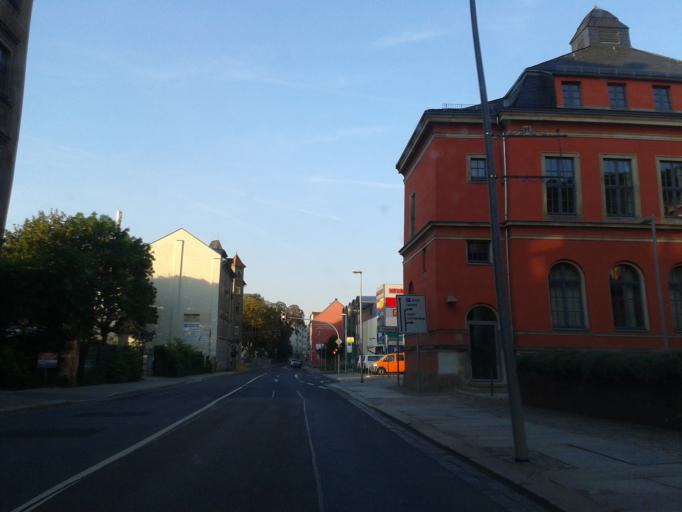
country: DE
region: Saxony
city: Meissen
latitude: 51.1577
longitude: 13.4705
